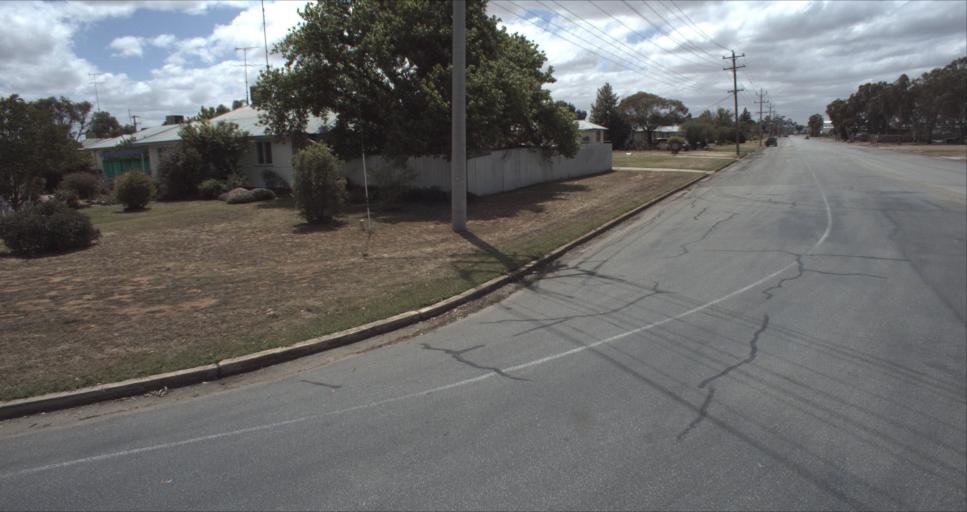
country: AU
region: New South Wales
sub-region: Leeton
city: Leeton
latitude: -34.5584
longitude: 146.3909
